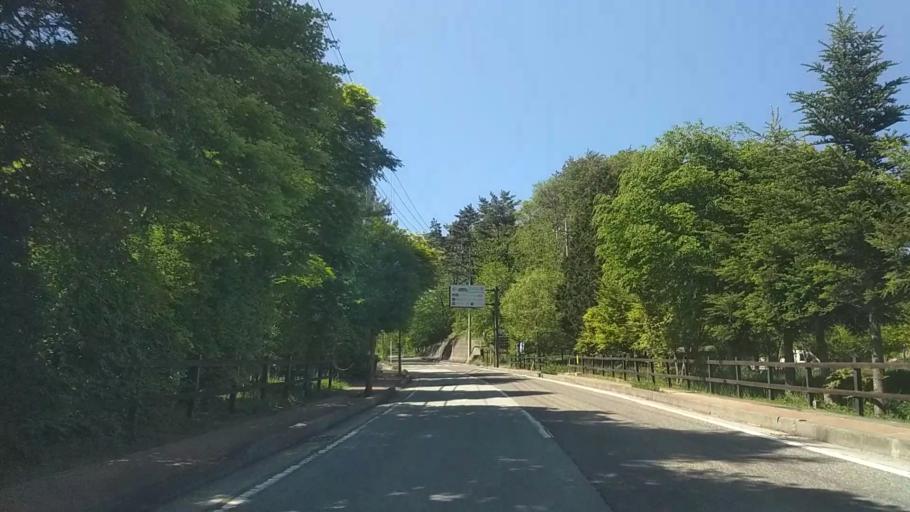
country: JP
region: Yamanashi
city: Nirasaki
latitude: 35.9037
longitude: 138.4352
